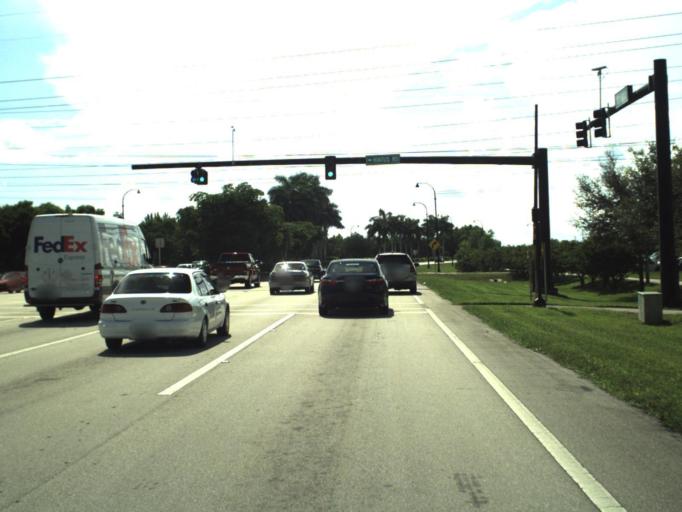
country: US
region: Florida
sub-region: Miami-Dade County
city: Country Club
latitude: 25.9842
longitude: -80.2995
